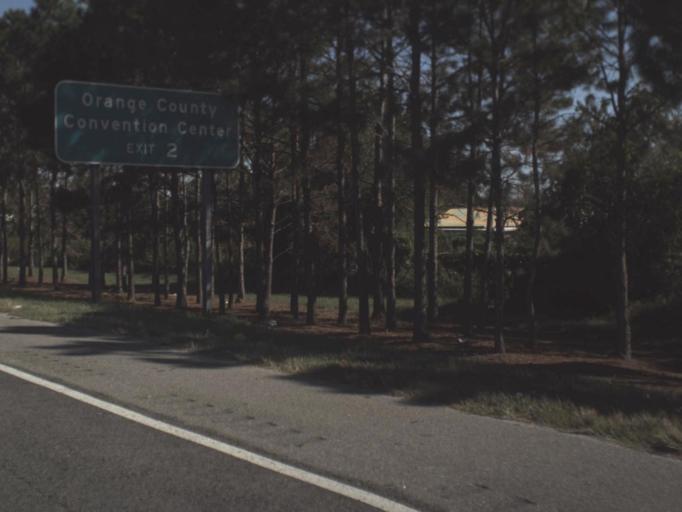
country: US
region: Florida
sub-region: Orange County
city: Williamsburg
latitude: 28.4210
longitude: -81.4523
